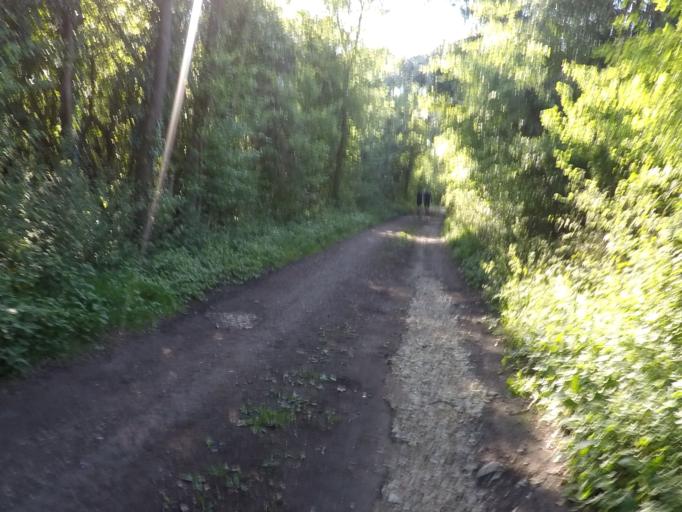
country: GB
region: England
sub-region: Oxfordshire
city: Charlbury
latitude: 51.8749
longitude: -1.4687
